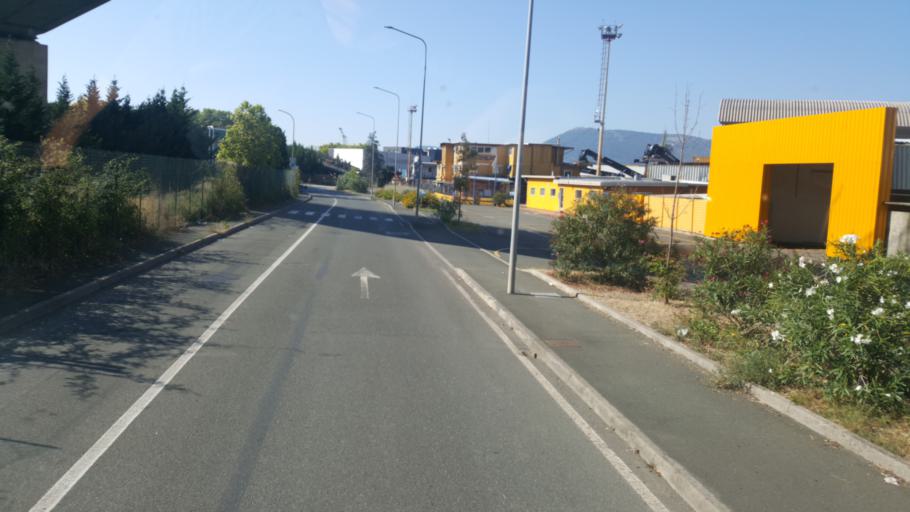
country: IT
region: Liguria
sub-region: Provincia di La Spezia
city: La Spezia
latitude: 44.1076
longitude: 9.8611
